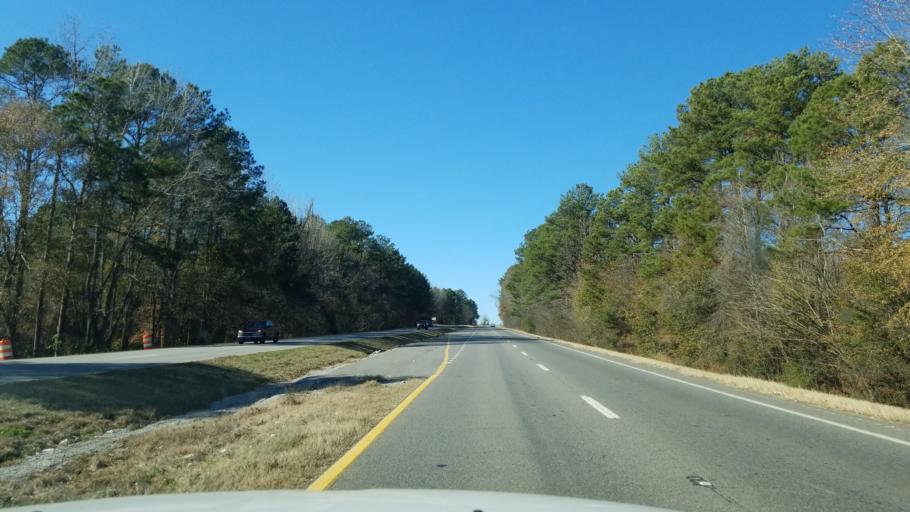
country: US
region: Alabama
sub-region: Tuscaloosa County
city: Northport
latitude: 33.2479
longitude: -87.6779
